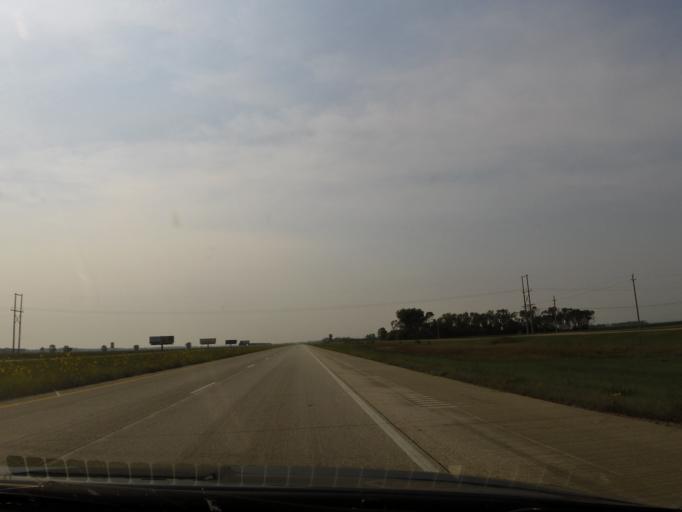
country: US
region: North Dakota
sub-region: Cass County
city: Horace
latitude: 46.7761
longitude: -96.8395
